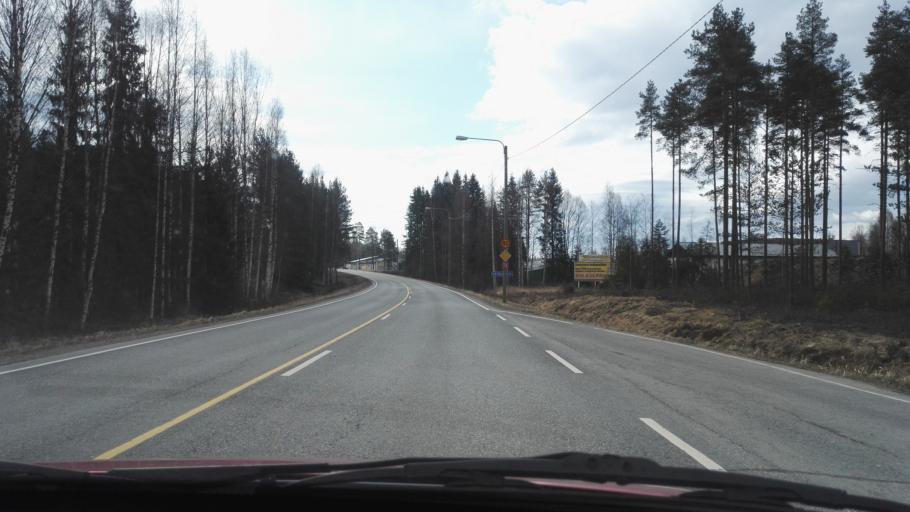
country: FI
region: Central Finland
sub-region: Jyvaeskylae
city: Petaejaevesi
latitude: 62.2672
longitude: 25.1720
